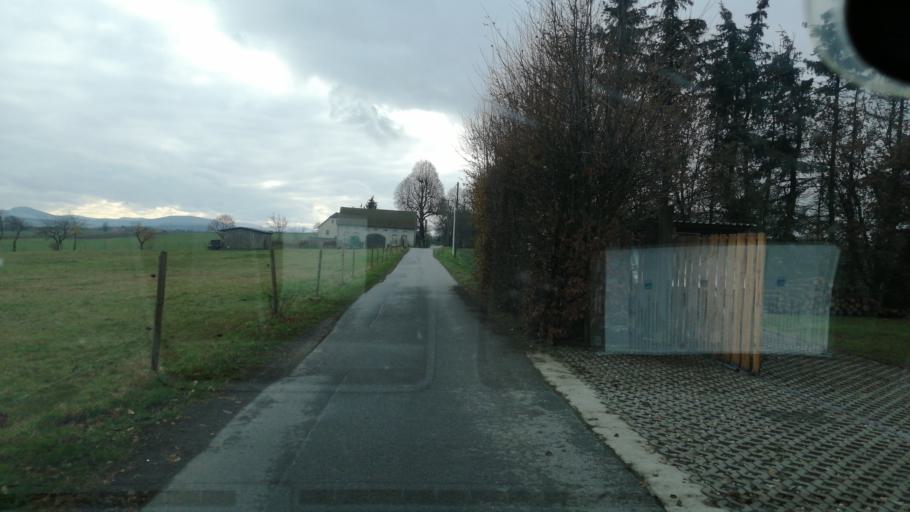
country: DE
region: Saxony
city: Bernstadt
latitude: 51.0557
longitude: 14.7974
